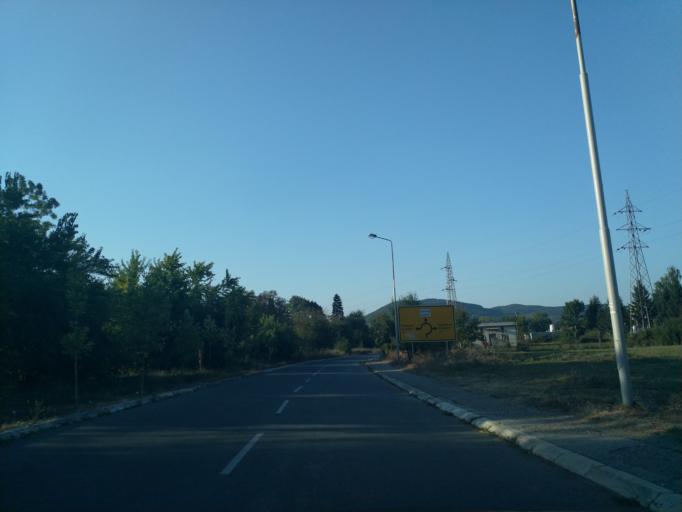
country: RS
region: Central Serbia
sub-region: Rasinski Okrug
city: Trstenik
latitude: 43.6110
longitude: 21.0071
